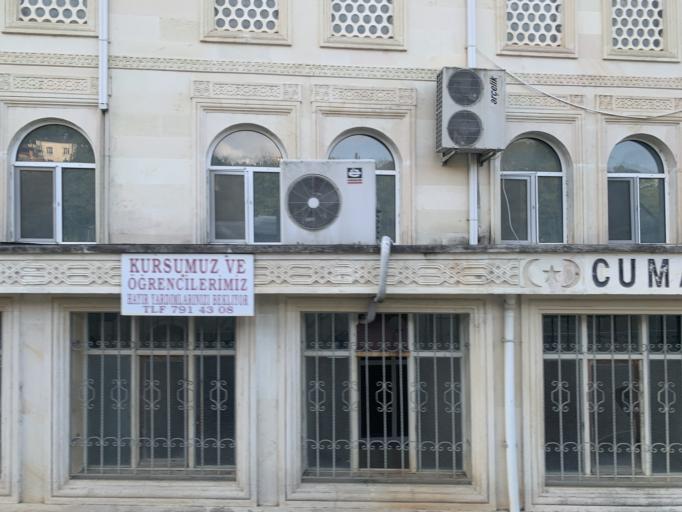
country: TR
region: Trabzon
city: Dernekpazari
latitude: 40.8314
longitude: 40.2694
